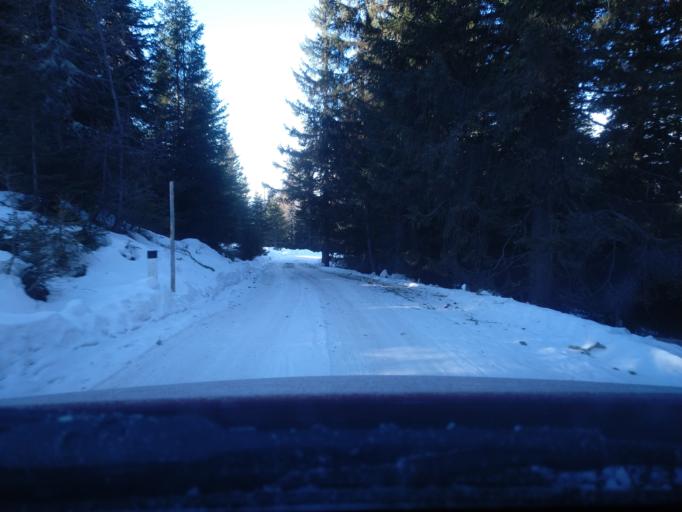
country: AT
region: Carinthia
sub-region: Politischer Bezirk Villach Land
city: Arriach
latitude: 46.6977
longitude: 13.9027
